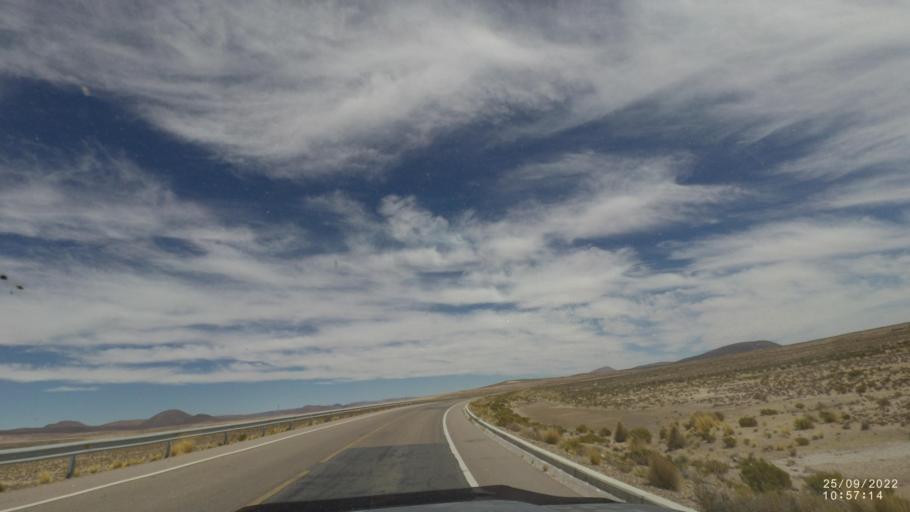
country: BO
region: Oruro
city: Challapata
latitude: -19.4767
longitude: -66.8878
